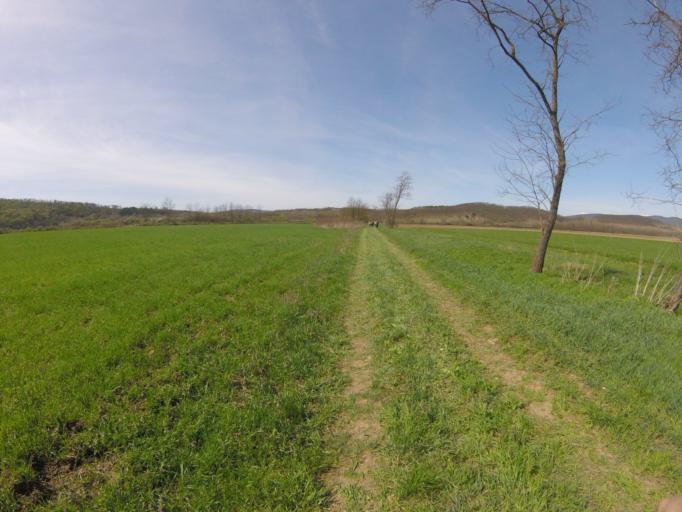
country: HU
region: Borsod-Abauj-Zemplen
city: Szendro
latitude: 48.4179
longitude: 20.7645
